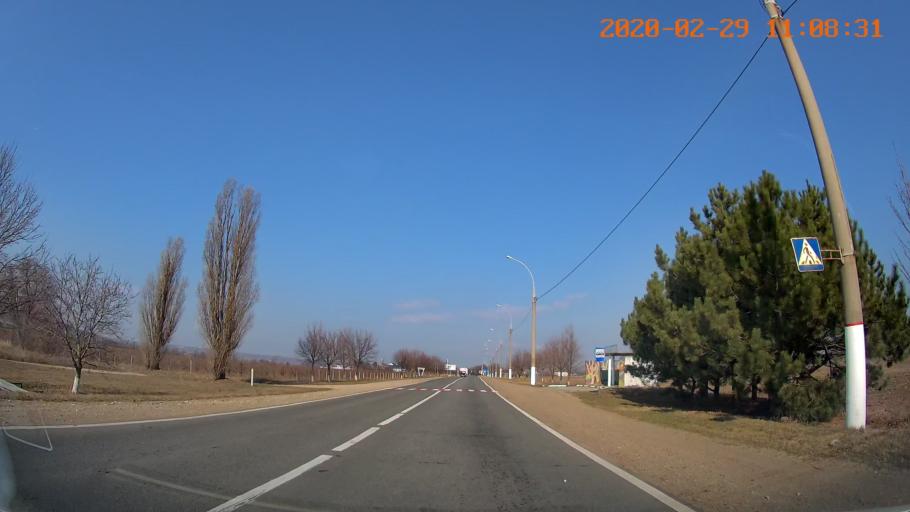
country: MD
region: Criuleni
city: Criuleni
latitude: 47.2349
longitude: 29.1751
